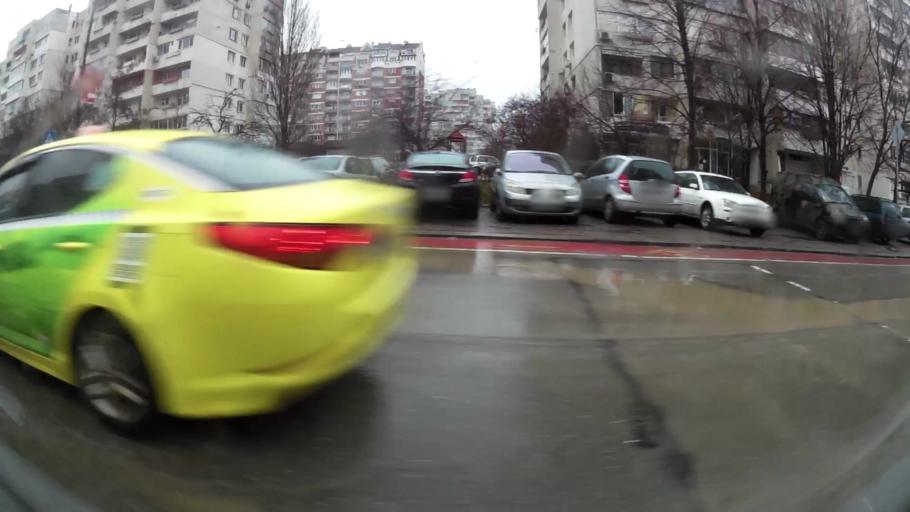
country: BG
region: Sofia-Capital
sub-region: Stolichna Obshtina
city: Sofia
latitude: 42.6332
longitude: 23.3749
